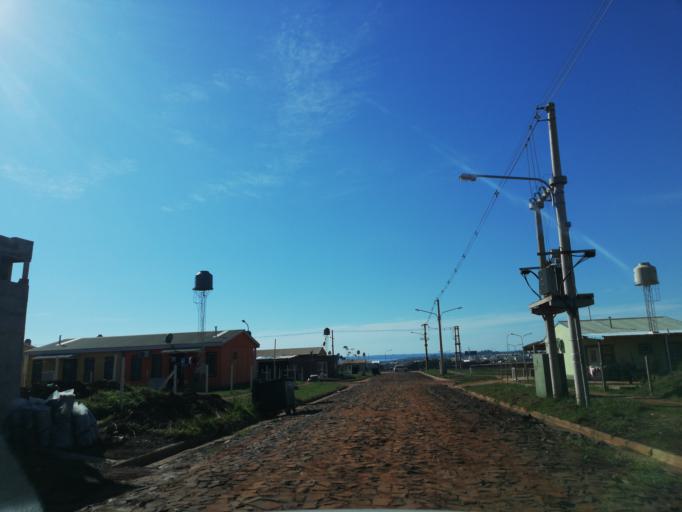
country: AR
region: Misiones
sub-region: Departamento de Capital
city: Posadas
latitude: -27.4155
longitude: -55.9895
